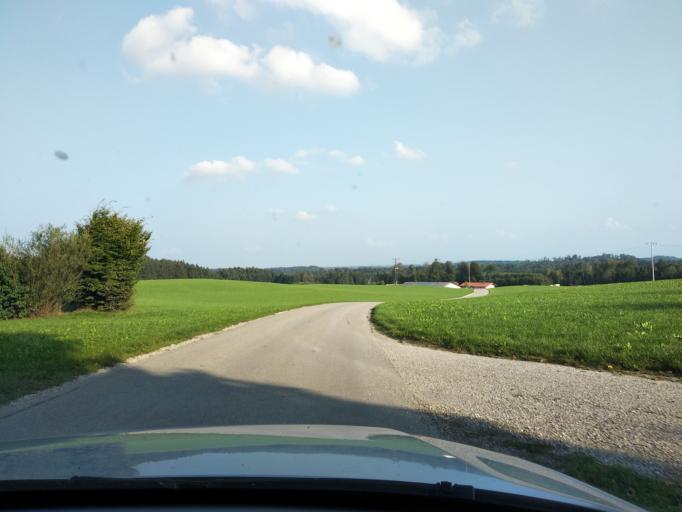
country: DE
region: Bavaria
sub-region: Upper Bavaria
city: Obing
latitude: 47.9927
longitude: 12.4324
